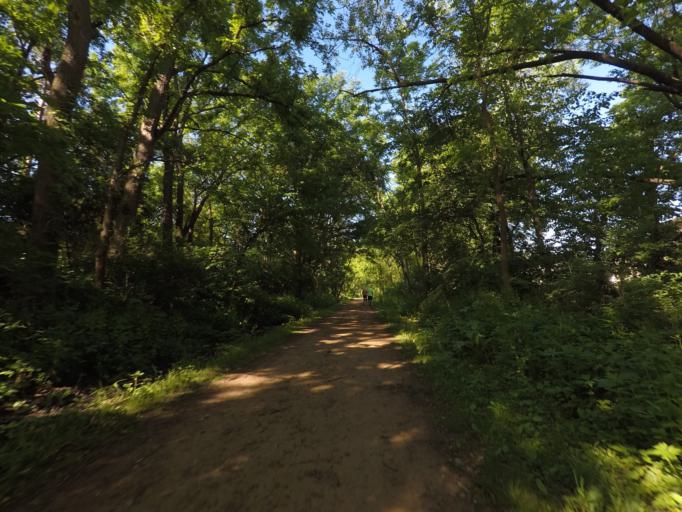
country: US
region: Wisconsin
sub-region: Dane County
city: Verona
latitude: 42.9855
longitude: -89.5365
